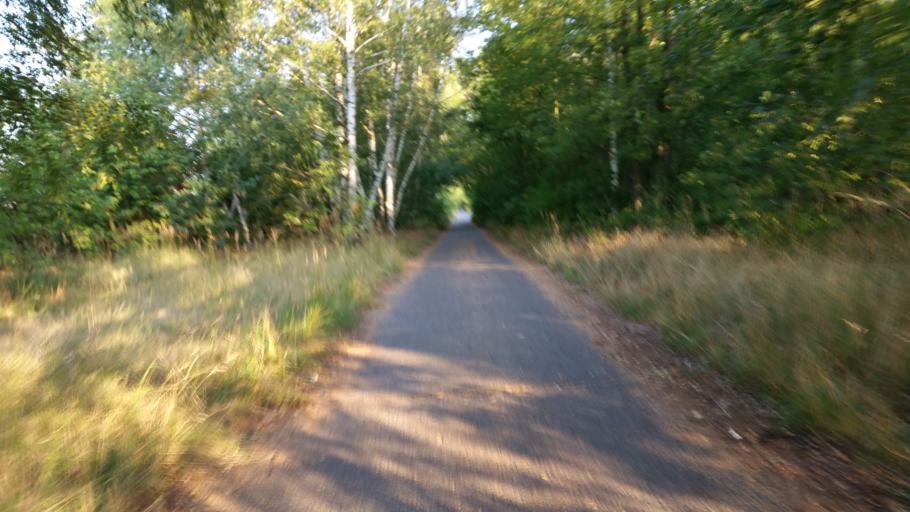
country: DE
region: Berlin
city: Marienfelde
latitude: 52.4050
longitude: 13.3466
